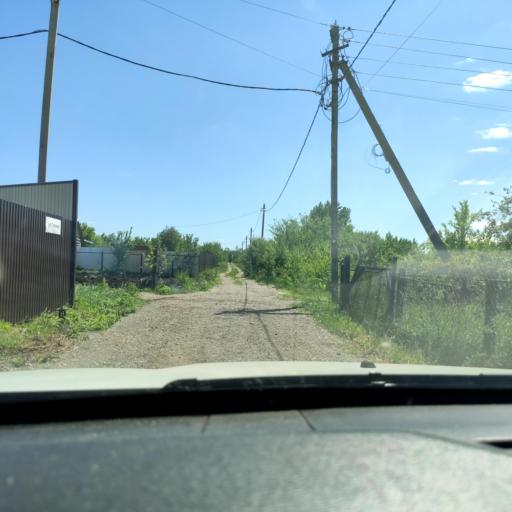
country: RU
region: Samara
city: Dubovyy Umet
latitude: 53.0270
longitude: 50.2500
